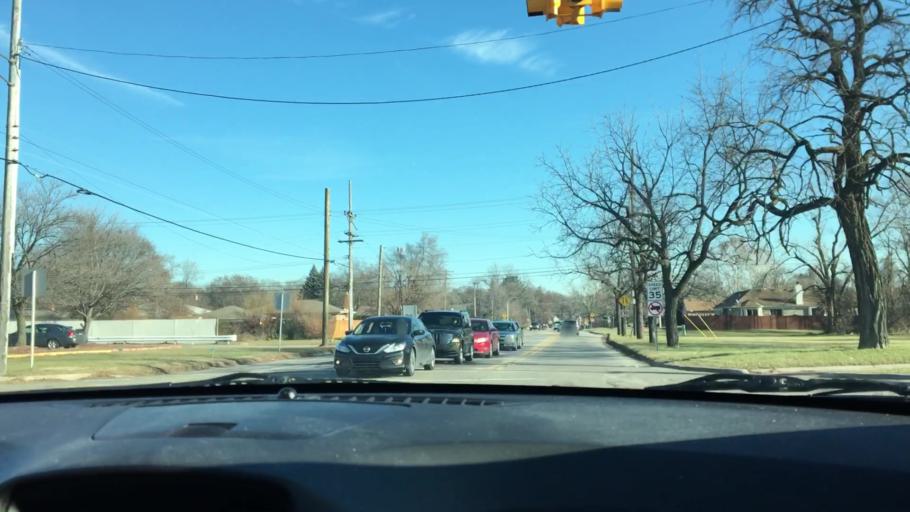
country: US
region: Michigan
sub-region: Wayne County
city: Westland
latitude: 42.3560
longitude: -83.3863
